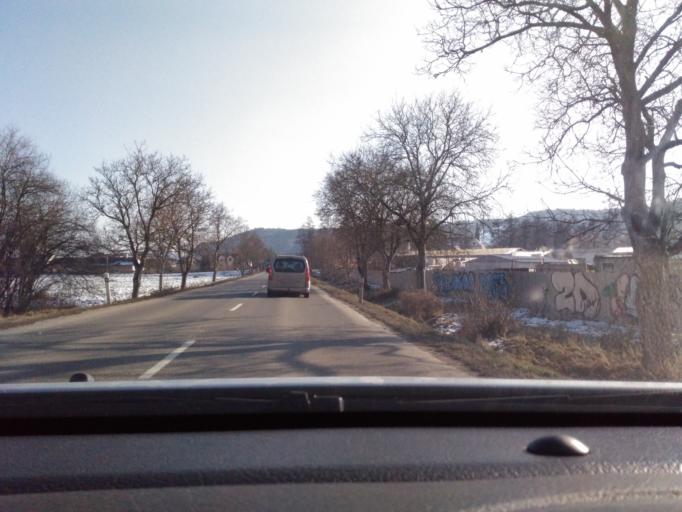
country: CZ
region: South Moravian
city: Predklasteri
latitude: 49.3584
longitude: 16.4001
